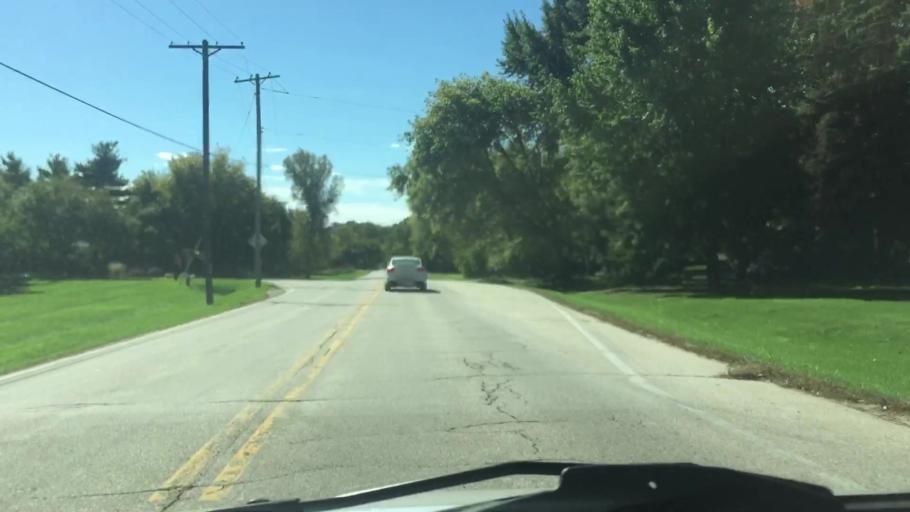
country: US
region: Wisconsin
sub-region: Waukesha County
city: Pewaukee
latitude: 43.0603
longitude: -88.2827
